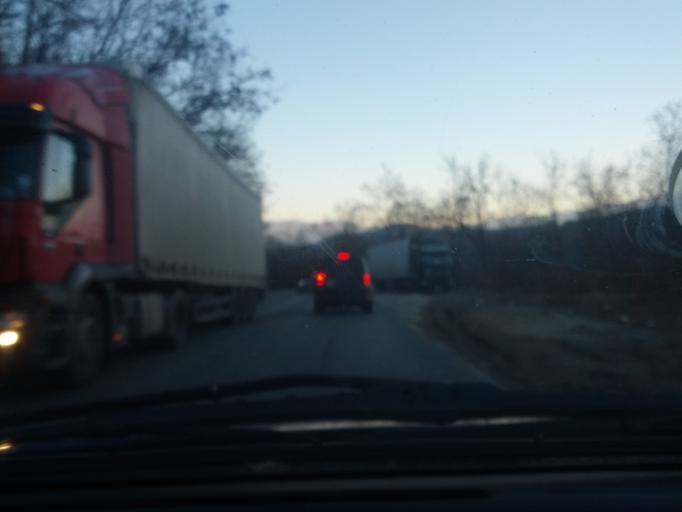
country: BG
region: Vratsa
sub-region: Obshtina Mezdra
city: Mezdra
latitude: 43.0192
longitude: 23.6861
